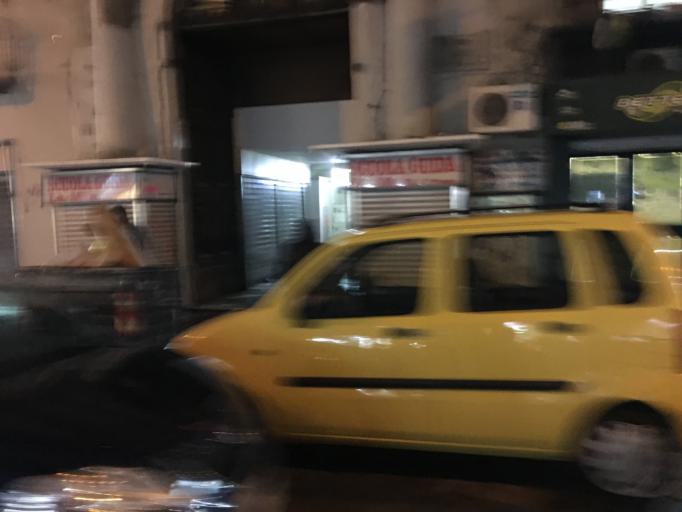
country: IT
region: Campania
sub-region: Provincia di Napoli
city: Napoli
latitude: 40.8501
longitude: 14.2685
